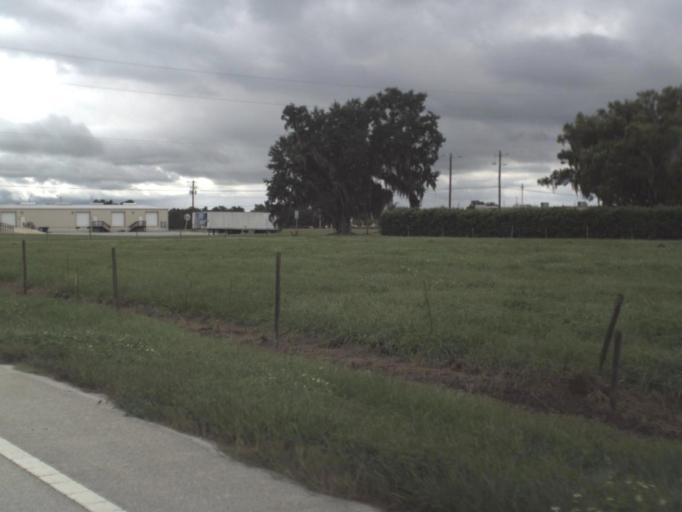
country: US
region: Florida
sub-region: Hardee County
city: Bowling Green
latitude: 27.5949
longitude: -81.8349
